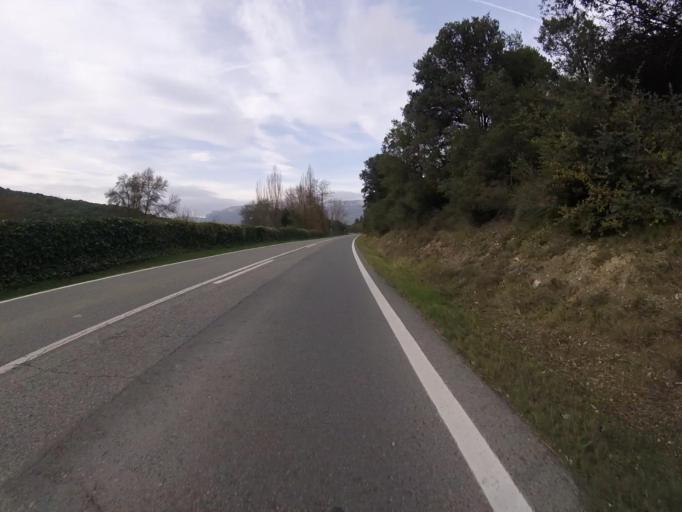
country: ES
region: Navarre
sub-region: Provincia de Navarra
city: Estella
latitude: 42.7017
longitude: -2.0598
